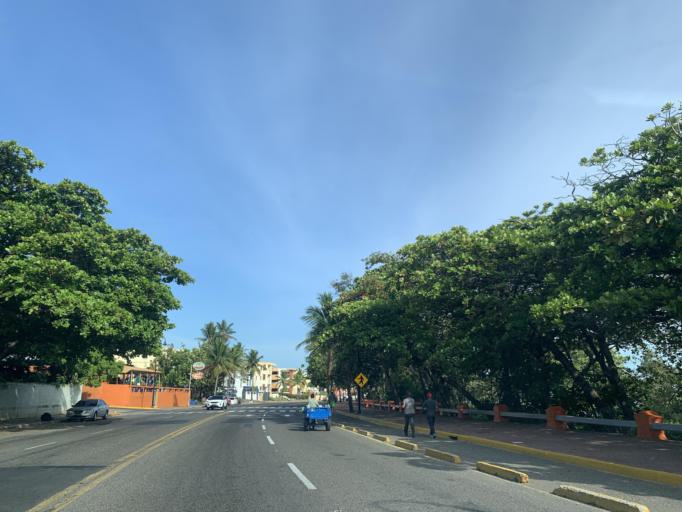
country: DO
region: Puerto Plata
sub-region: Puerto Plata
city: Puerto Plata
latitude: 19.7980
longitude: -70.6876
